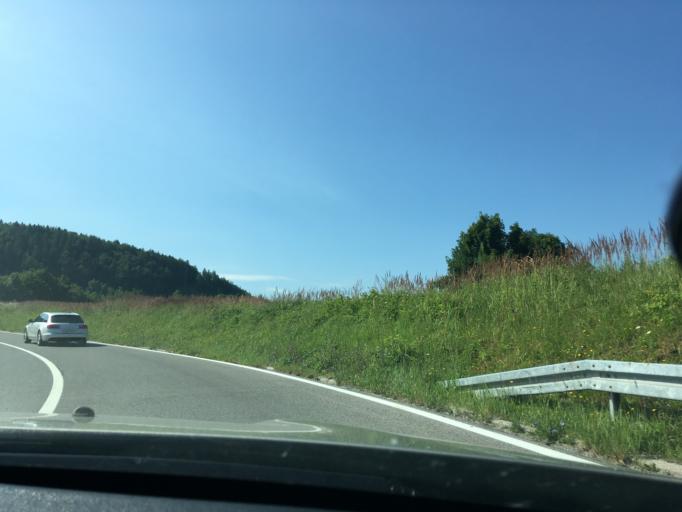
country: HR
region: Primorsko-Goranska
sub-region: Grad Delnice
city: Delnice
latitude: 45.4024
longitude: 14.8081
